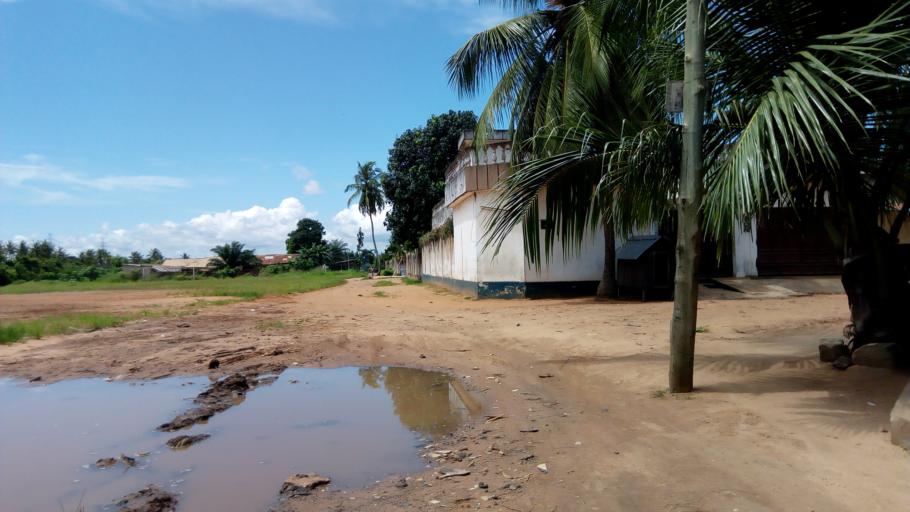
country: TG
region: Maritime
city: Lome
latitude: 6.1701
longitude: 1.1808
